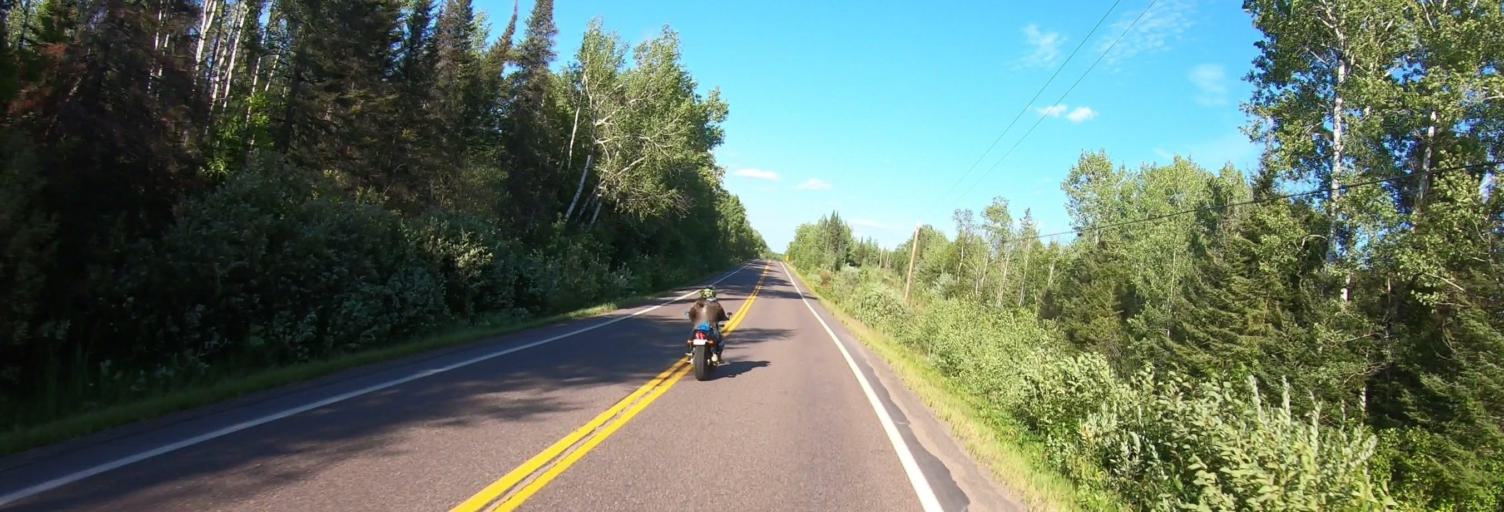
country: US
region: Minnesota
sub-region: Saint Louis County
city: Ely
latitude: 47.9601
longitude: -91.5724
